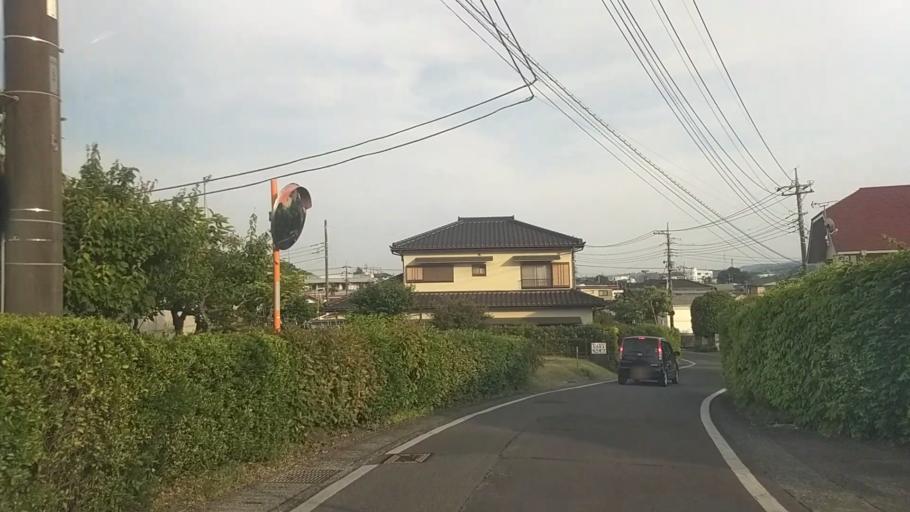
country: JP
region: Kanagawa
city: Odawara
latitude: 35.3161
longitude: 139.1162
